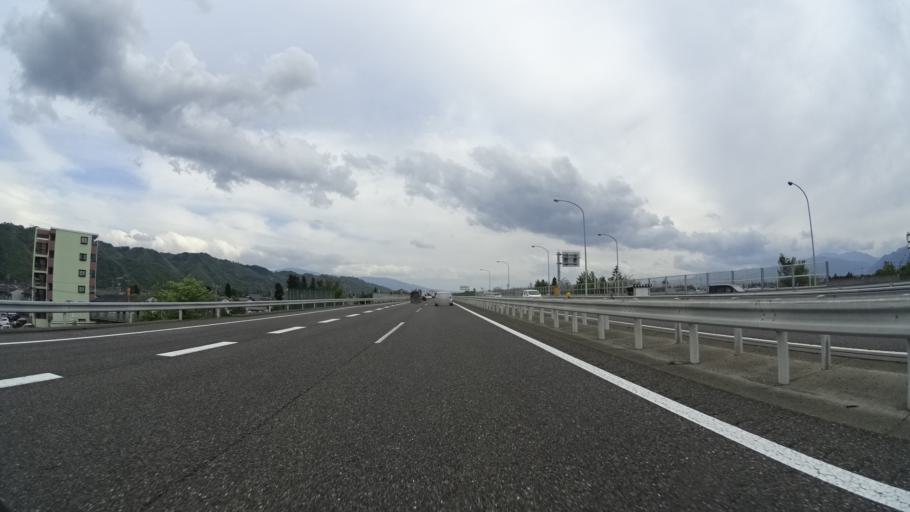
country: JP
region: Nagano
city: Toyoshina
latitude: 36.2977
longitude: 137.9258
